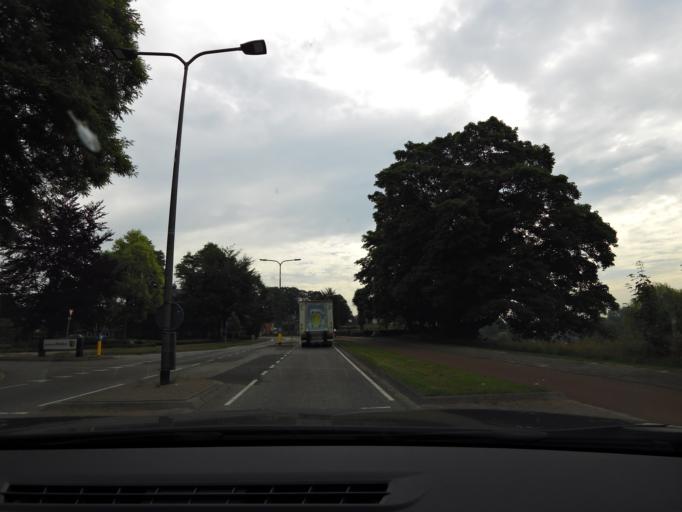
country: NL
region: Gelderland
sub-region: Gemeente Rheden
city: De Steeg
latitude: 52.0174
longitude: 6.0570
